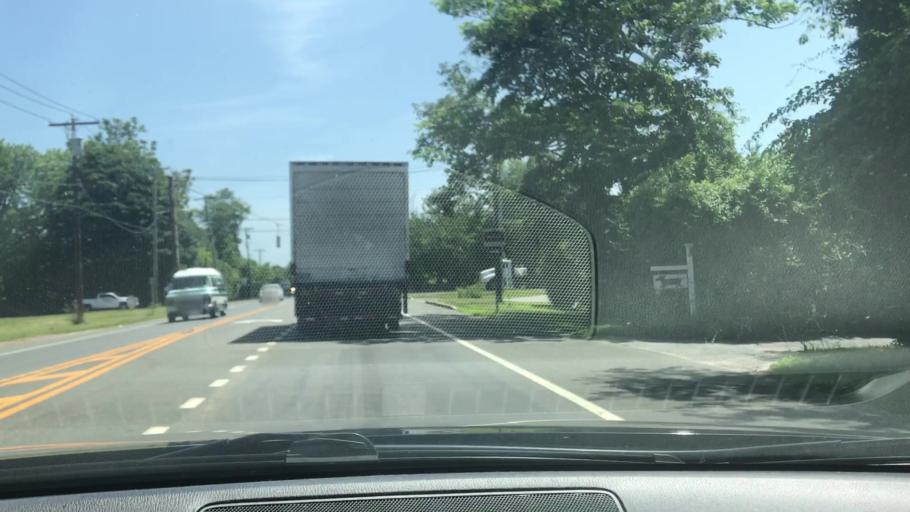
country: US
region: New York
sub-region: Suffolk County
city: Bridgehampton
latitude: 40.9410
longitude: -72.2799
